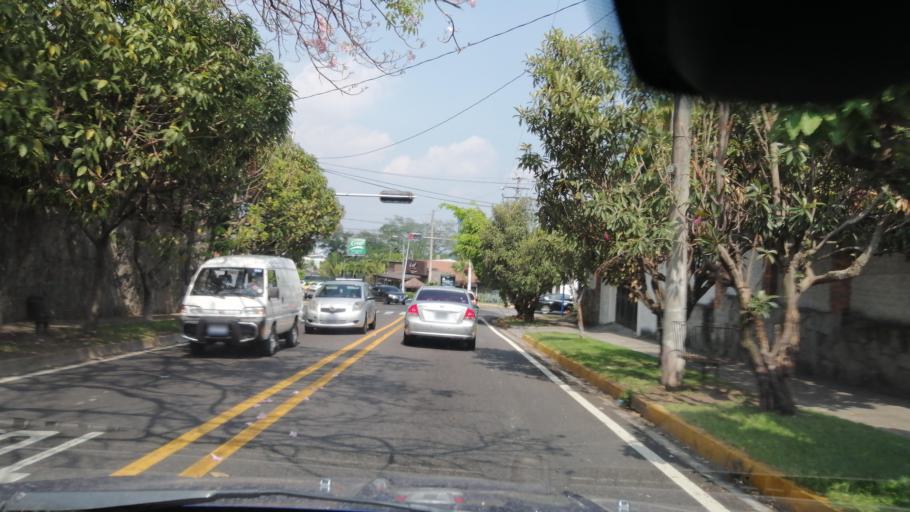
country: SV
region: La Libertad
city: Antiguo Cuscatlan
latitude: 13.6989
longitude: -89.2425
